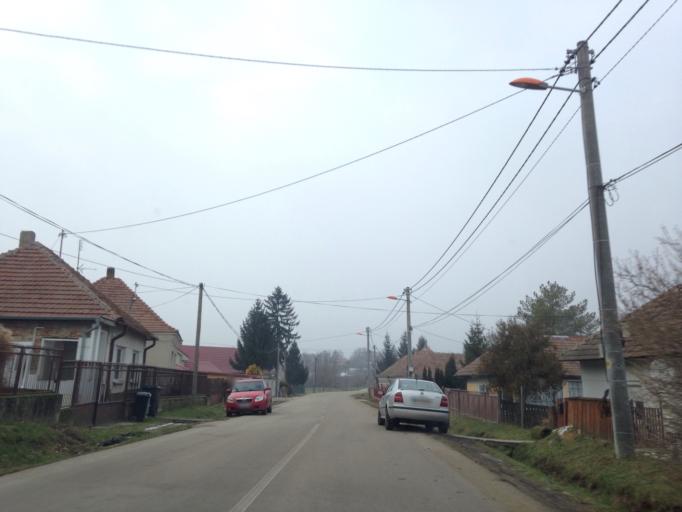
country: SK
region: Nitriansky
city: Svodin
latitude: 48.0062
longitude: 18.3616
